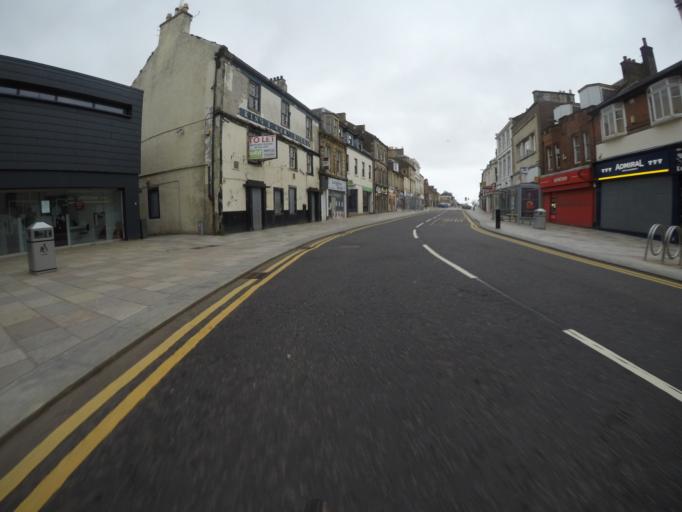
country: GB
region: Scotland
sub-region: North Ayrshire
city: Irvine
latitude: 55.6149
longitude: -4.6673
